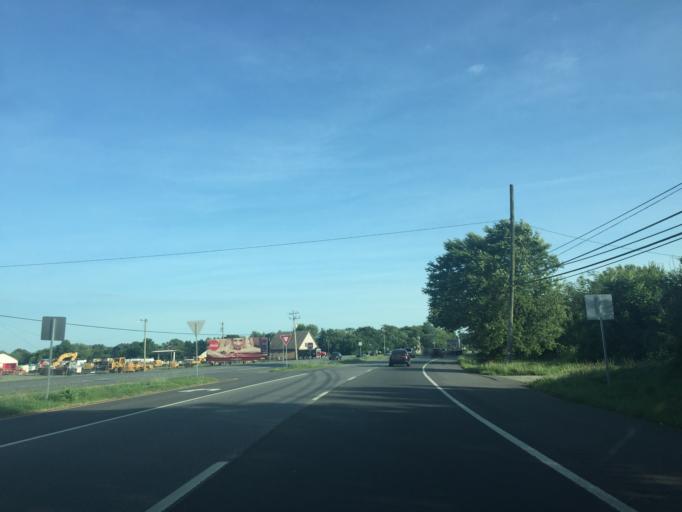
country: US
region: Delaware
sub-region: Kent County
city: Smyrna
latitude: 39.2647
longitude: -75.5869
